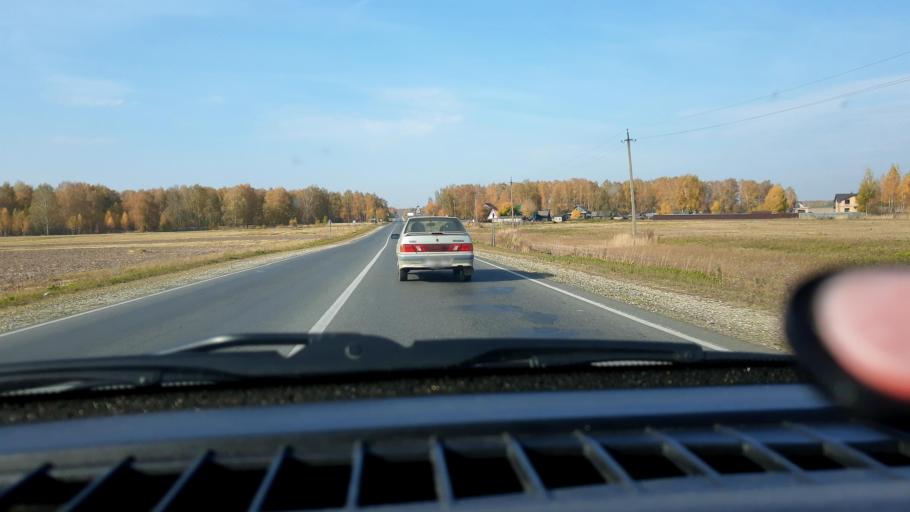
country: RU
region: Nizjnij Novgorod
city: Gorodets
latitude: 56.6279
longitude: 43.5437
